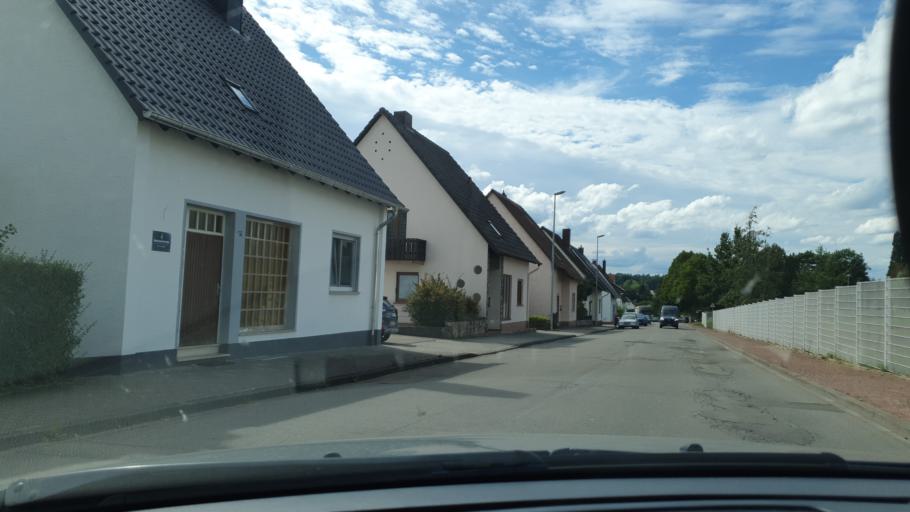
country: DE
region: Rheinland-Pfalz
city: Zweibrucken
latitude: 49.2390
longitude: 7.3687
